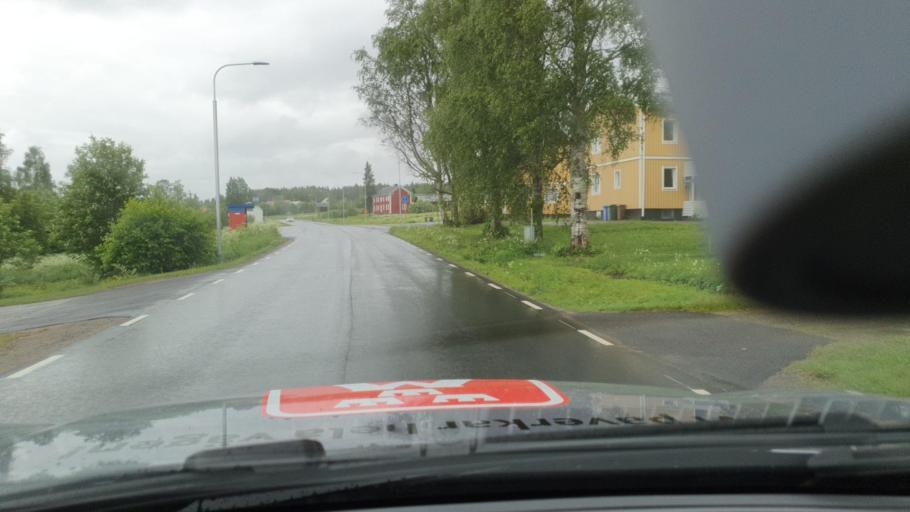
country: FI
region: Lapland
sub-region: Torniolaakso
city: Ylitornio
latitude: 66.2333
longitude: 23.6814
